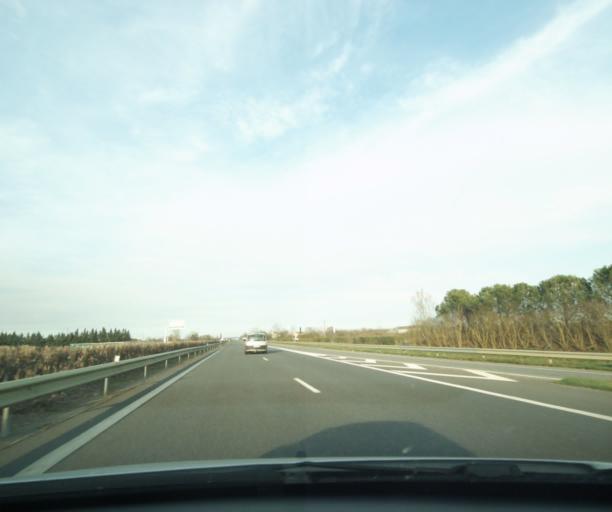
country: FR
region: Midi-Pyrenees
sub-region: Departement de la Haute-Garonne
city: Rieux-Volvestre
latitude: 43.2750
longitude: 1.1405
